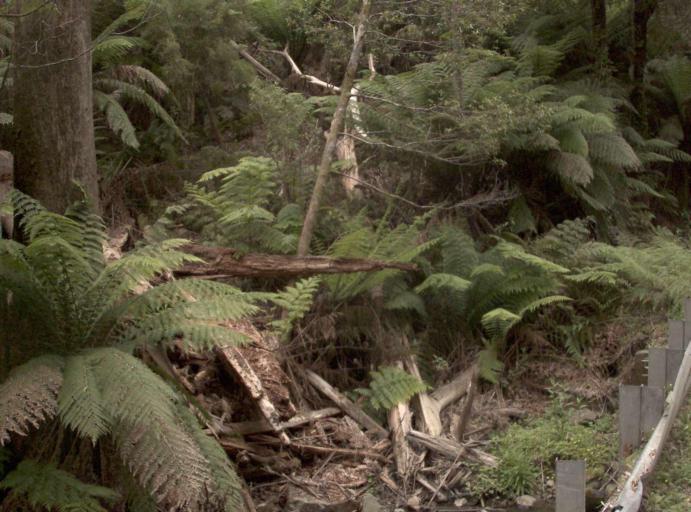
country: AU
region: Victoria
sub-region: Latrobe
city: Traralgon
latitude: -38.4505
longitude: 146.5393
